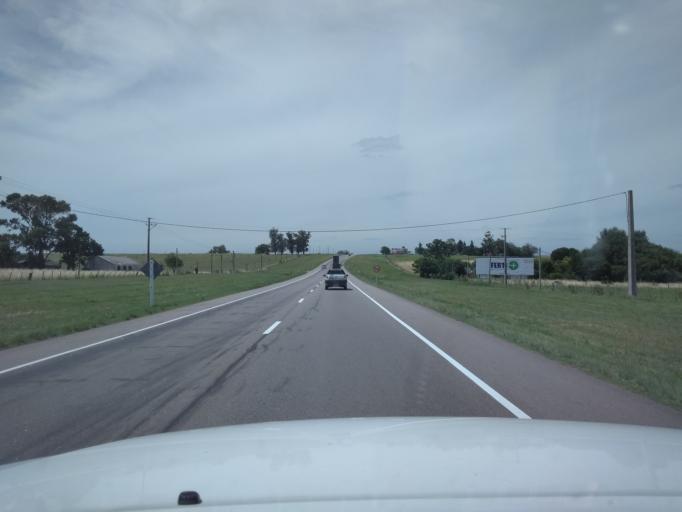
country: UY
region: Florida
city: Florida
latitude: -34.1730
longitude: -56.1886
